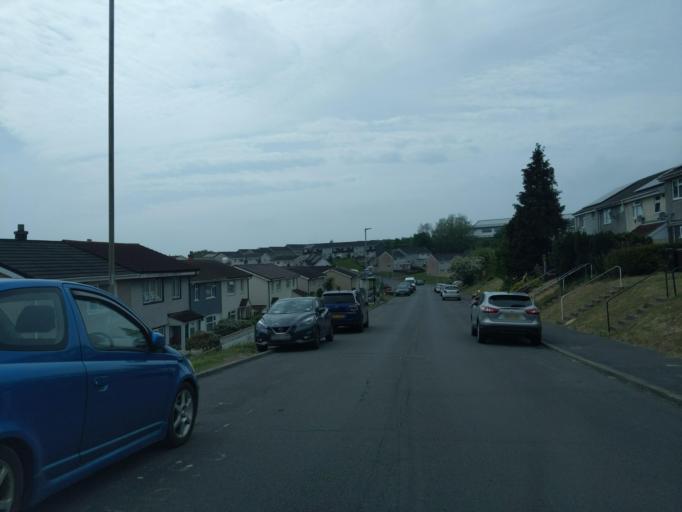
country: GB
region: England
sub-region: Cornwall
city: Torpoint
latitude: 50.4066
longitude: -4.1714
